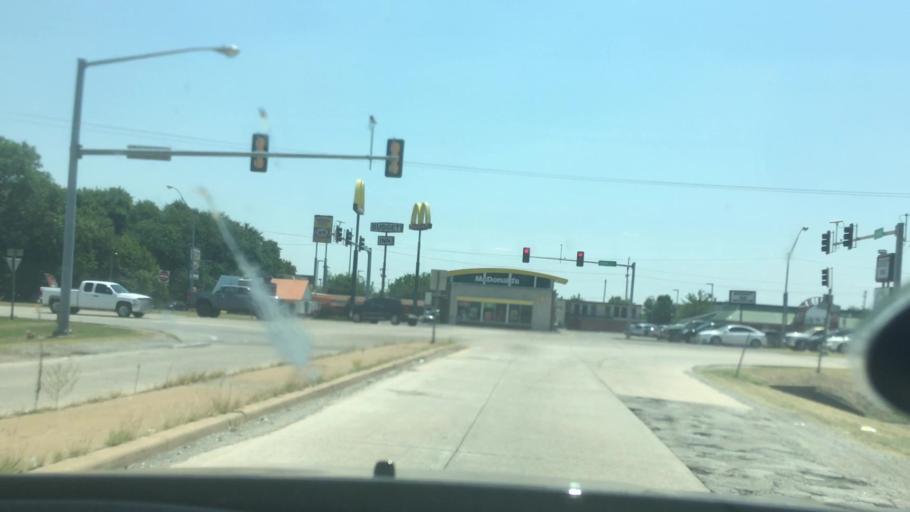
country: US
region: Oklahoma
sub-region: Bryan County
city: Durant
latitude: 33.9988
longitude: -96.4056
